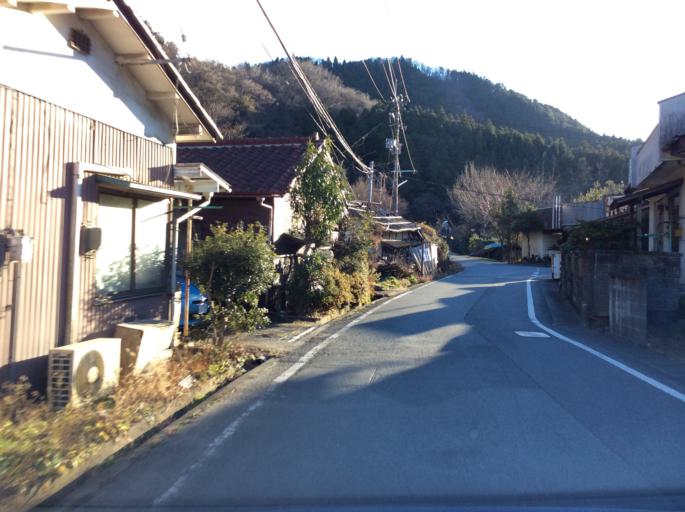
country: JP
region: Ibaraki
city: Kitaibaraki
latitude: 36.9033
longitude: 140.7323
